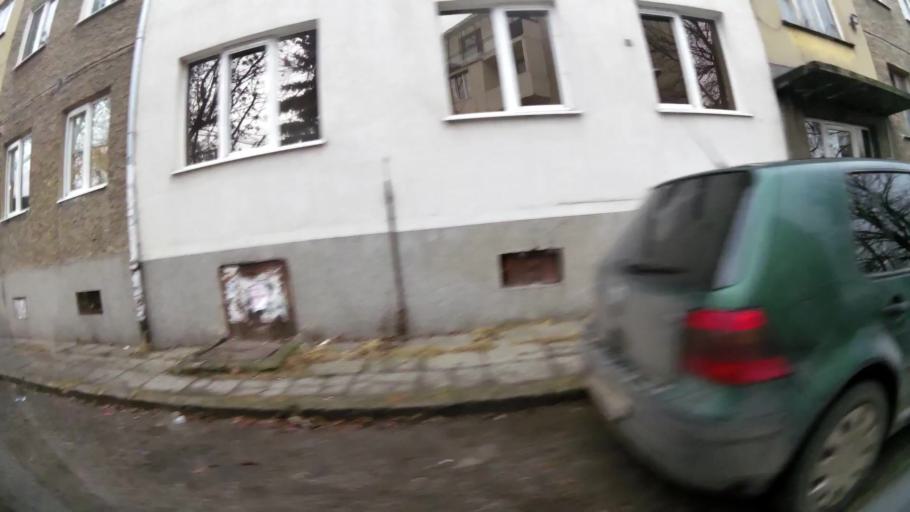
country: BG
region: Sofia-Capital
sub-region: Stolichna Obshtina
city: Sofia
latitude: 42.7338
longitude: 23.3075
